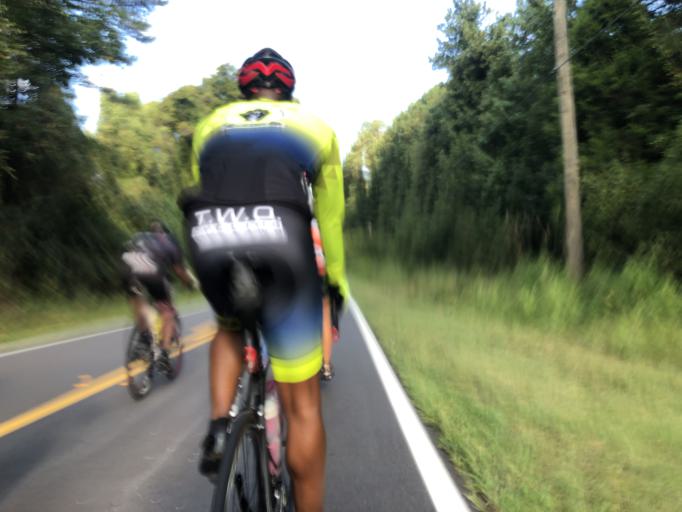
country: US
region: Georgia
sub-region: Fulton County
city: Palmetto
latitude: 33.5803
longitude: -84.6847
